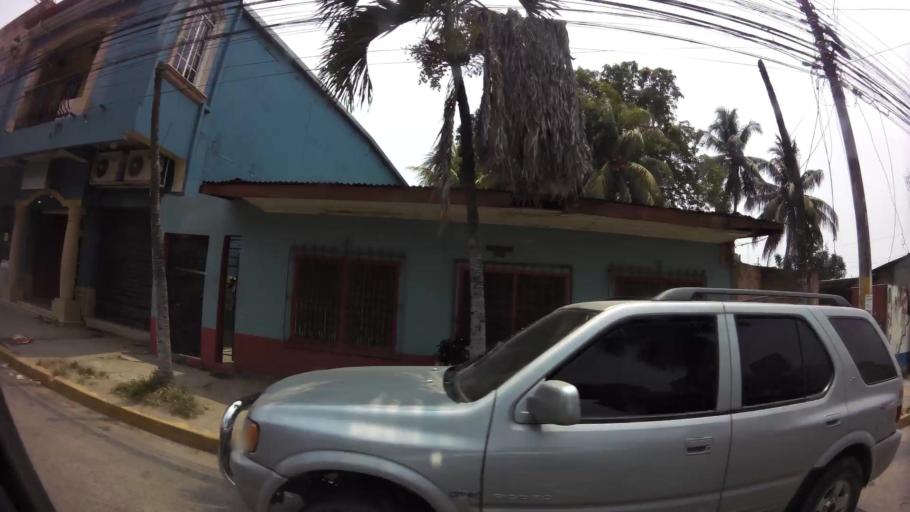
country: HN
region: Yoro
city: El Progreso
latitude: 15.4042
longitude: -87.8061
